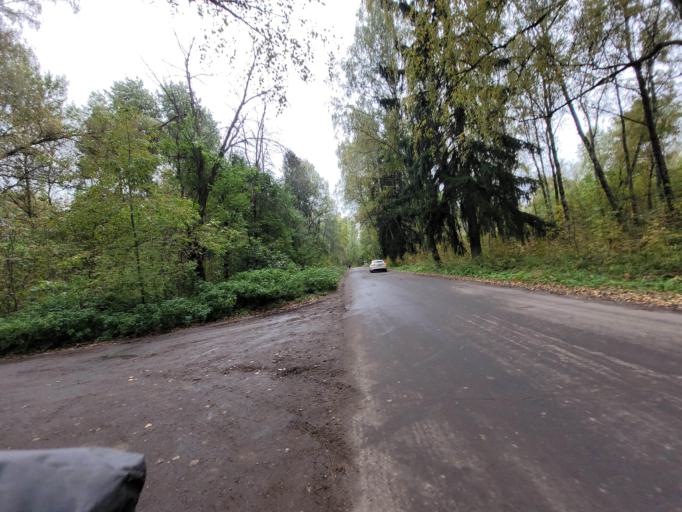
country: RU
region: Moscow
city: Babushkin
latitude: 55.8531
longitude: 37.7078
